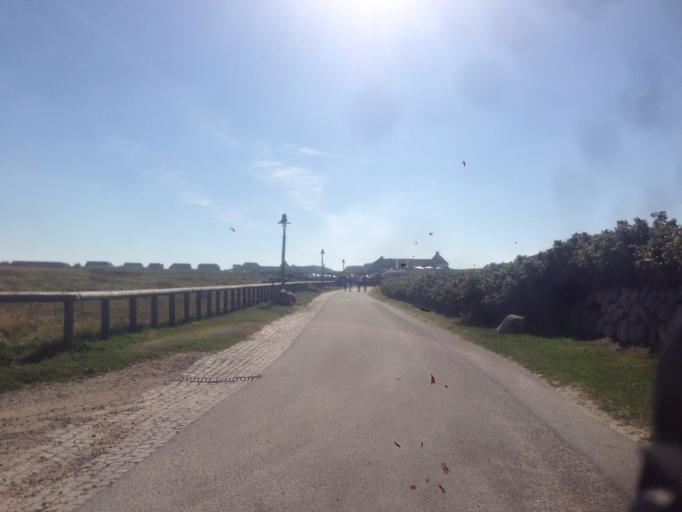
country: DE
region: Schleswig-Holstein
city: Westerland
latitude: 54.9641
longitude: 8.3351
